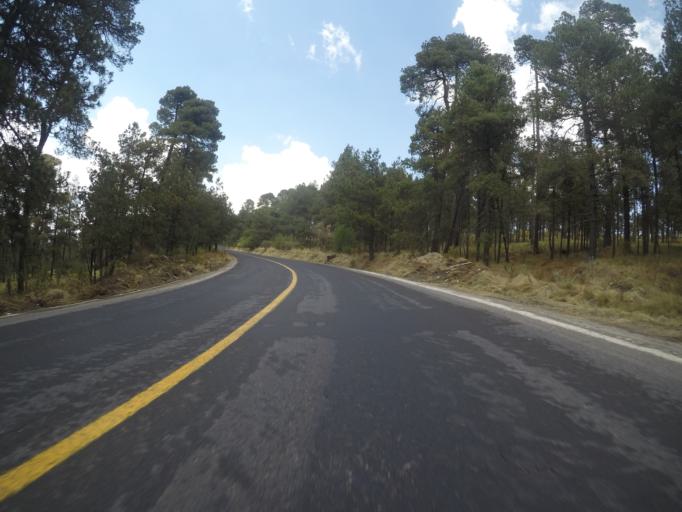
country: MX
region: Mexico
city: Cerro La Calera
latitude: 19.1333
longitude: -99.8145
